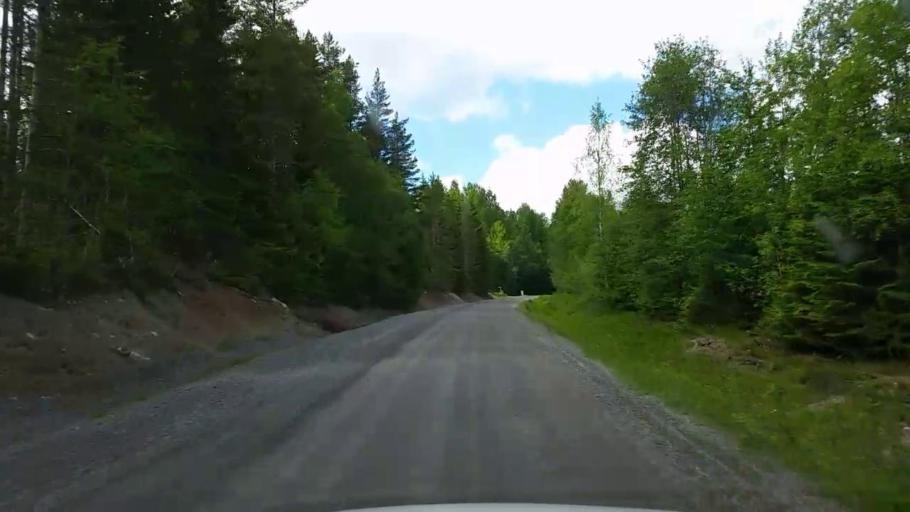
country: SE
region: Gaevleborg
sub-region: Bollnas Kommun
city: Vittsjo
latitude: 61.0928
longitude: 16.1713
